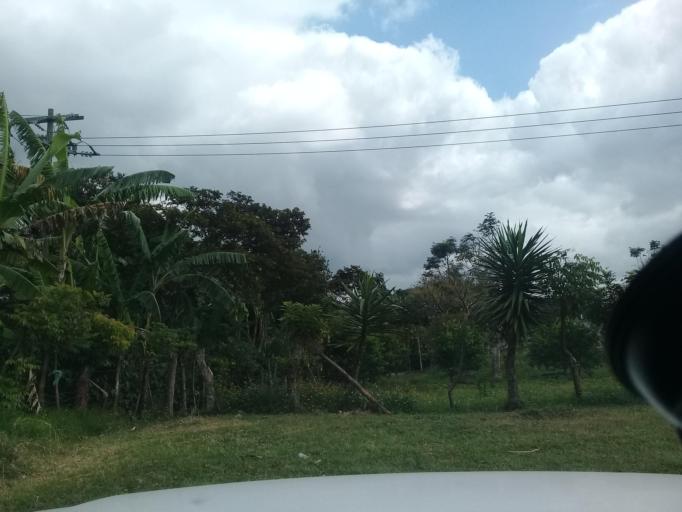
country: MX
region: Veracruz
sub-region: Xalapa
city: Fraccionamiento las Fuentes
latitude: 19.4725
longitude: -96.8788
